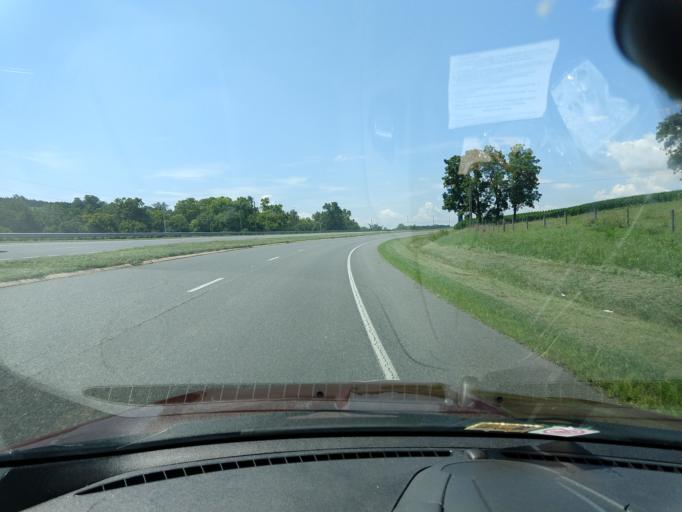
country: US
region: Virginia
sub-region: City of Harrisonburg
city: Harrisonburg
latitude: 38.5189
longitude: -78.8630
